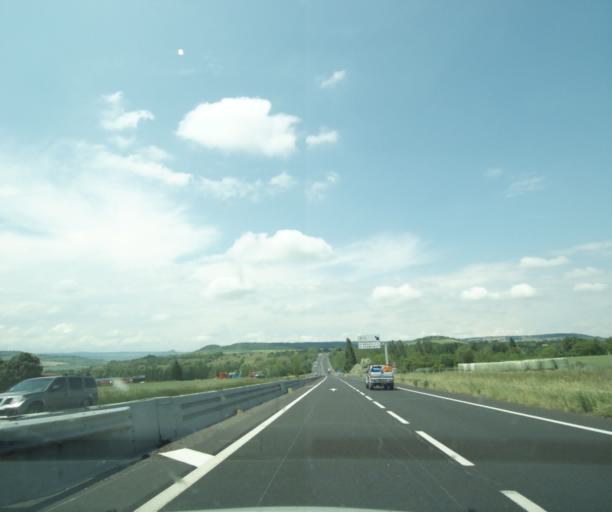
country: FR
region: Auvergne
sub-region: Departement du Puy-de-Dome
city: Le Breuil-sur-Couze
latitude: 45.4603
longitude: 3.2590
